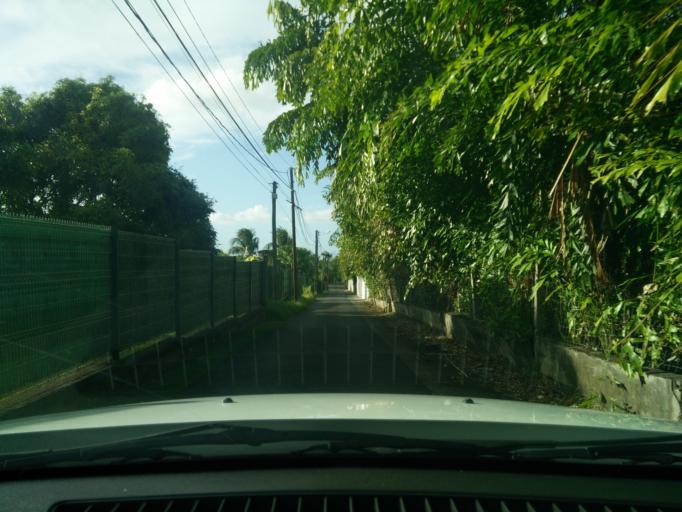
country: GP
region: Guadeloupe
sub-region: Guadeloupe
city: Baie-Mahault
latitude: 16.2553
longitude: -61.5846
